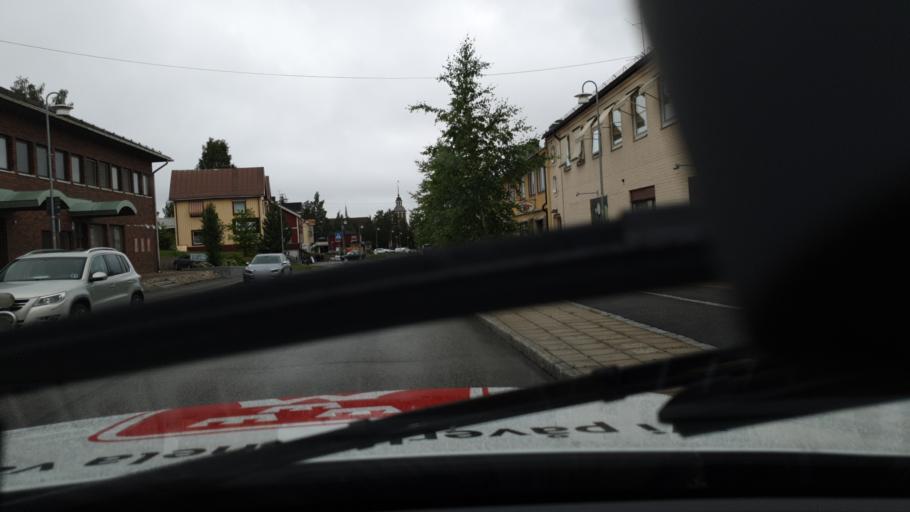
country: SE
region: Norrbotten
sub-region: Overtornea Kommun
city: OEvertornea
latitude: 66.3877
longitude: 23.6579
